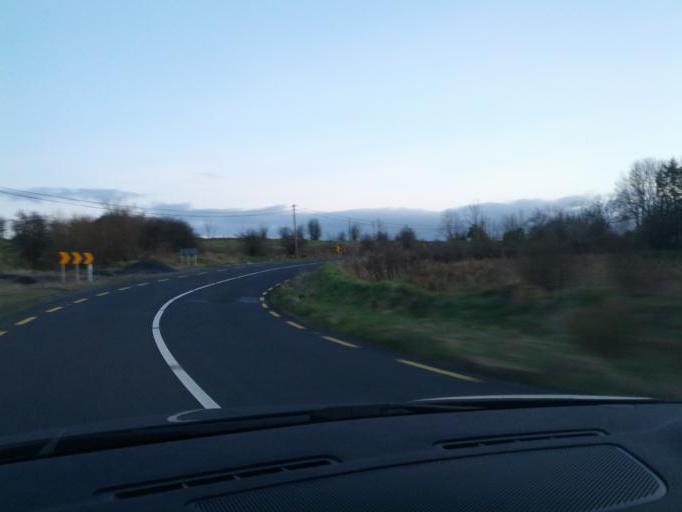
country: IE
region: Connaught
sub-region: Roscommon
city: Boyle
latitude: 53.9001
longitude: -8.2557
